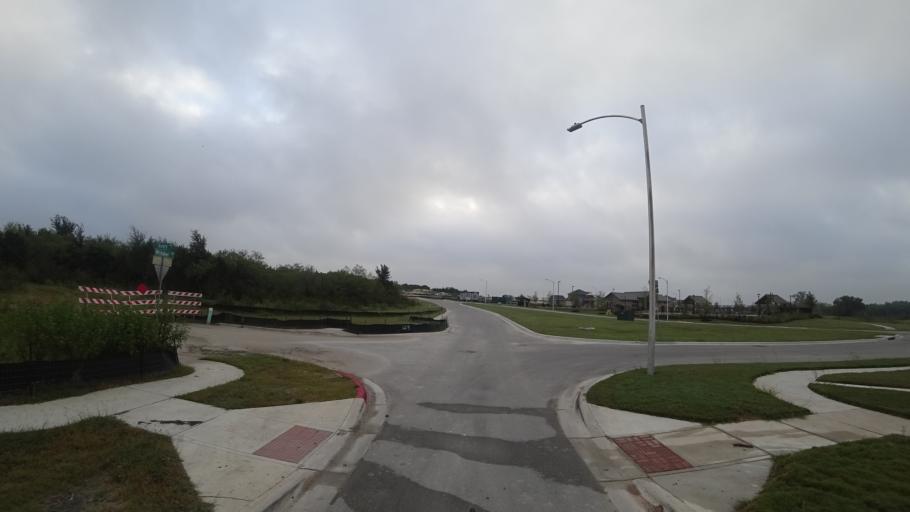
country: US
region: Texas
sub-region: Travis County
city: Wells Branch
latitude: 30.3588
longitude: -97.6668
